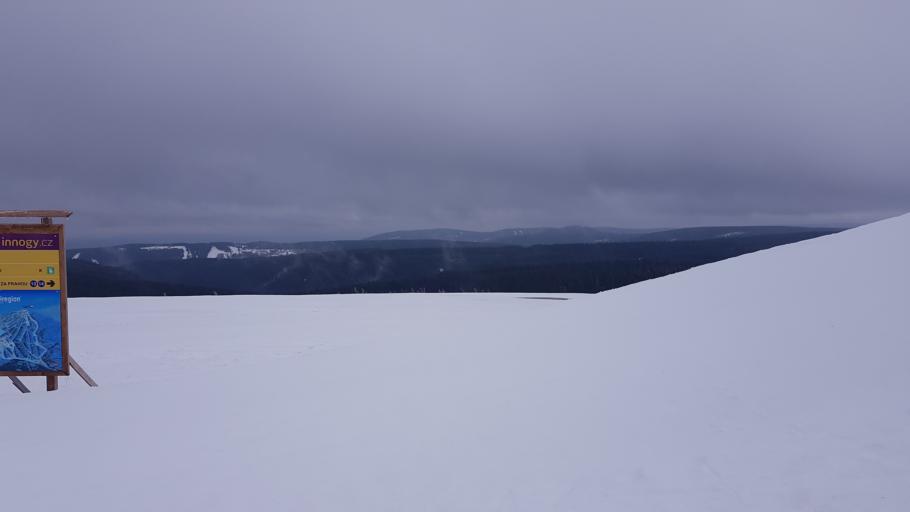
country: DE
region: Saxony
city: Kurort Oberwiesenthal
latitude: 50.4051
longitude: 12.9322
